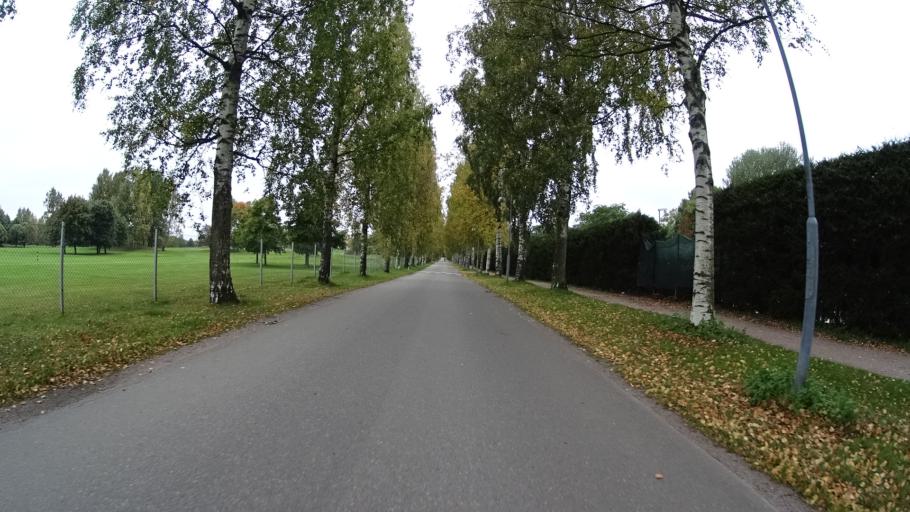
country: FI
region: Uusimaa
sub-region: Helsinki
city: Teekkarikylae
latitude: 60.2149
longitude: 24.8634
